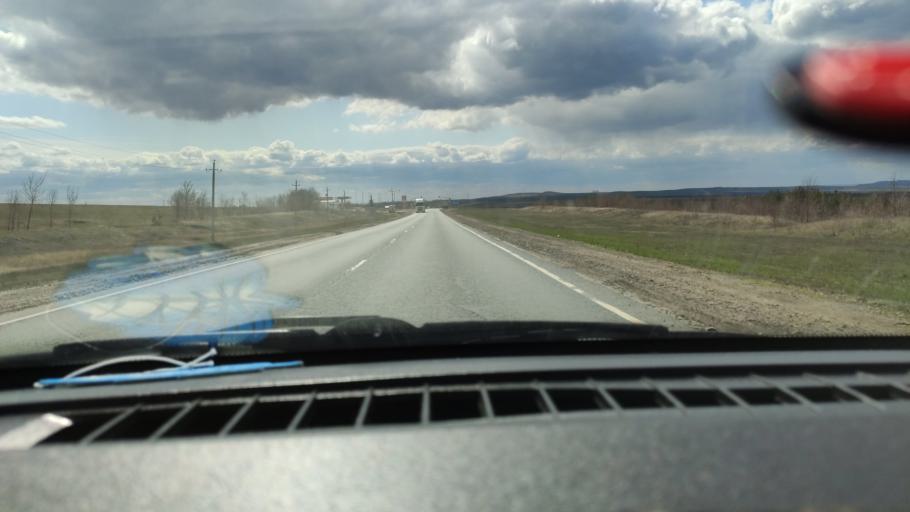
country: RU
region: Saratov
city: Alekseyevka
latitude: 52.2930
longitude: 47.9292
